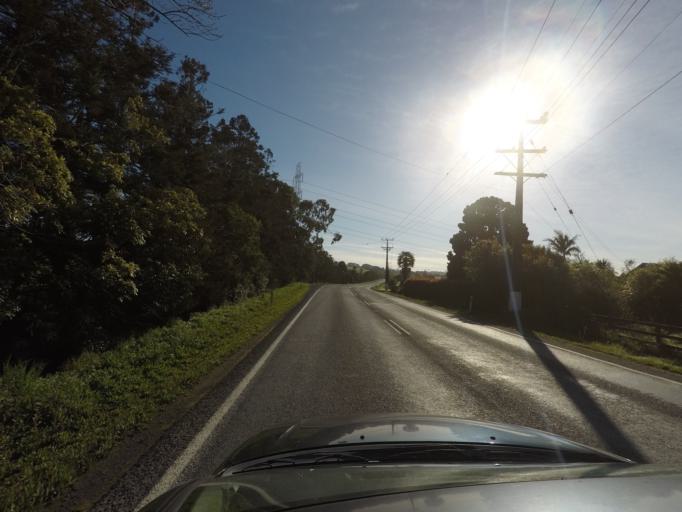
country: NZ
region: Auckland
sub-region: Auckland
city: Red Hill
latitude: -37.0017
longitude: 174.9600
